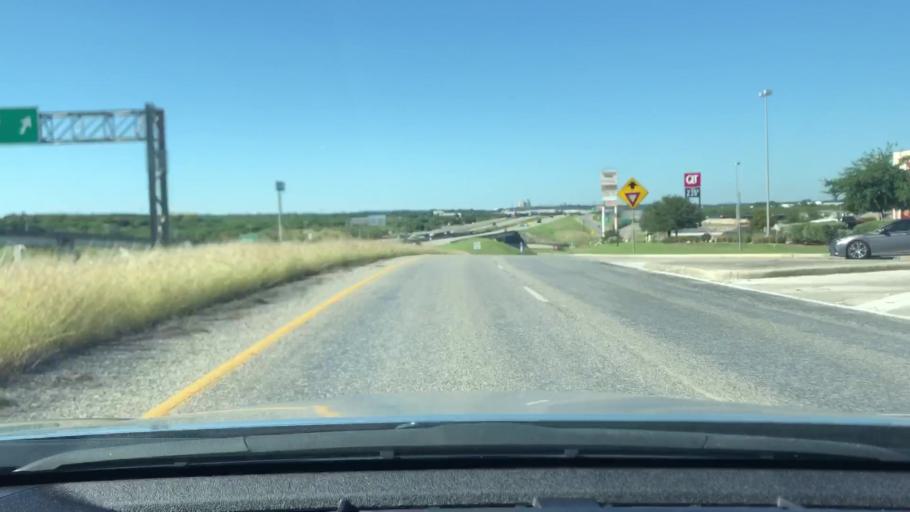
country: US
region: Texas
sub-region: Bexar County
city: Live Oak
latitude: 29.5758
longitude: -98.3401
